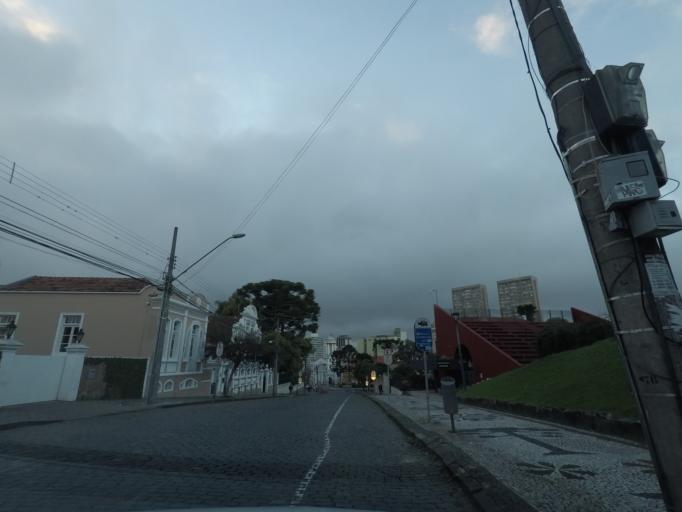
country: BR
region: Parana
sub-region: Curitiba
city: Curitiba
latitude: -25.4269
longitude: -49.2756
